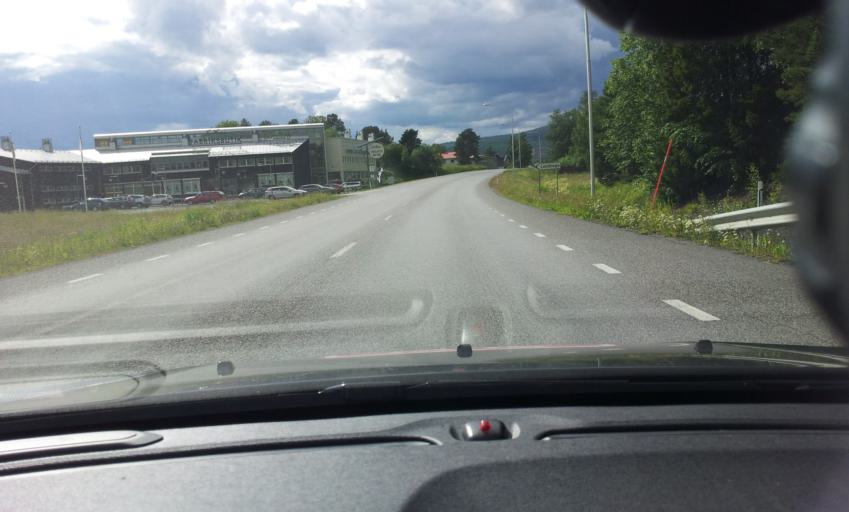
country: SE
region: Jaemtland
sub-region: Are Kommun
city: Jarpen
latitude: 63.3415
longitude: 13.4815
